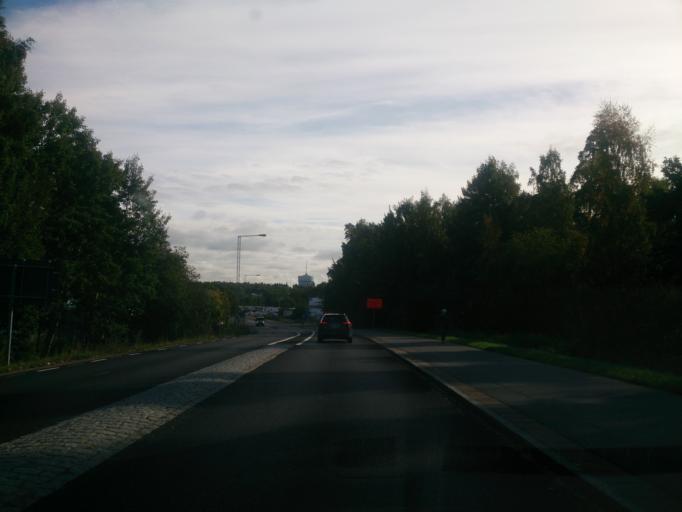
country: SE
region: OEstergoetland
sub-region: Linkopings Kommun
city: Linkoping
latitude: 58.3980
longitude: 15.6124
